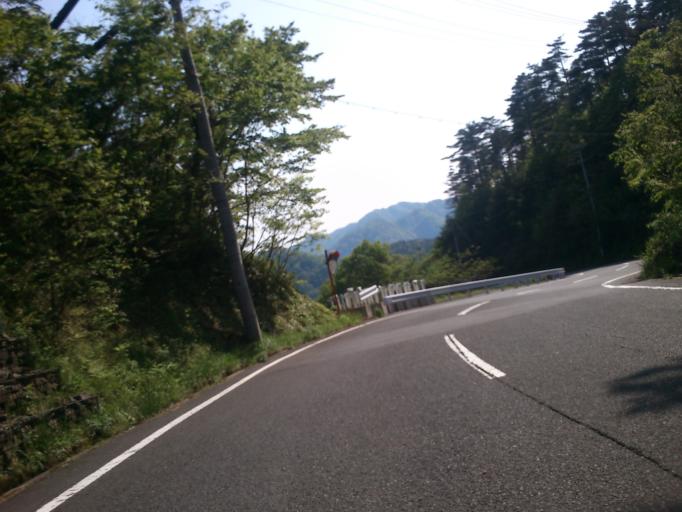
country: JP
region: Kyoto
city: Miyazu
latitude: 35.7339
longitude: 135.1790
